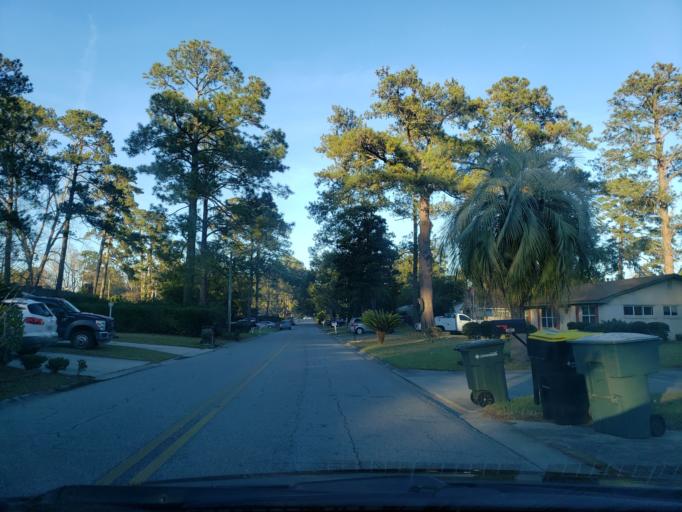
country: US
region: Georgia
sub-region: Chatham County
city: Isle of Hope
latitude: 31.9928
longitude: -81.1106
